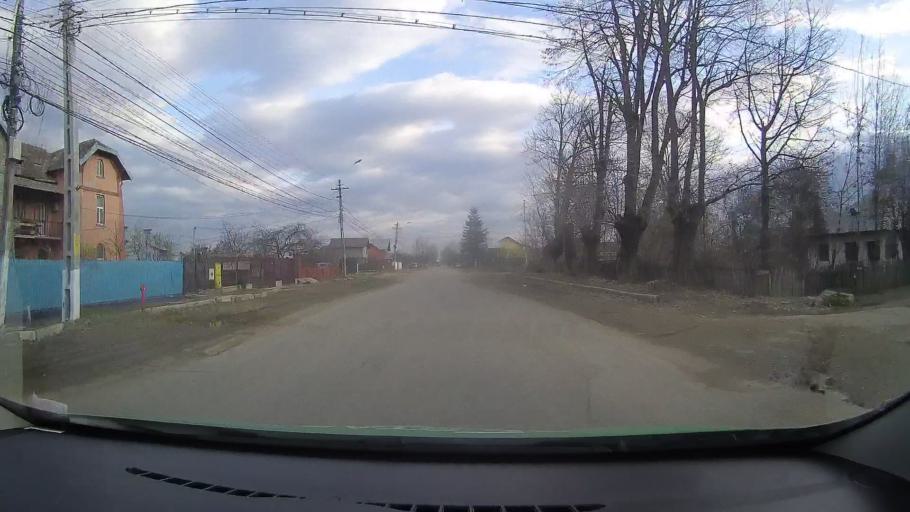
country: RO
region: Dambovita
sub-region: Municipiul Moreni
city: Moreni
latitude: 44.9684
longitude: 25.6527
